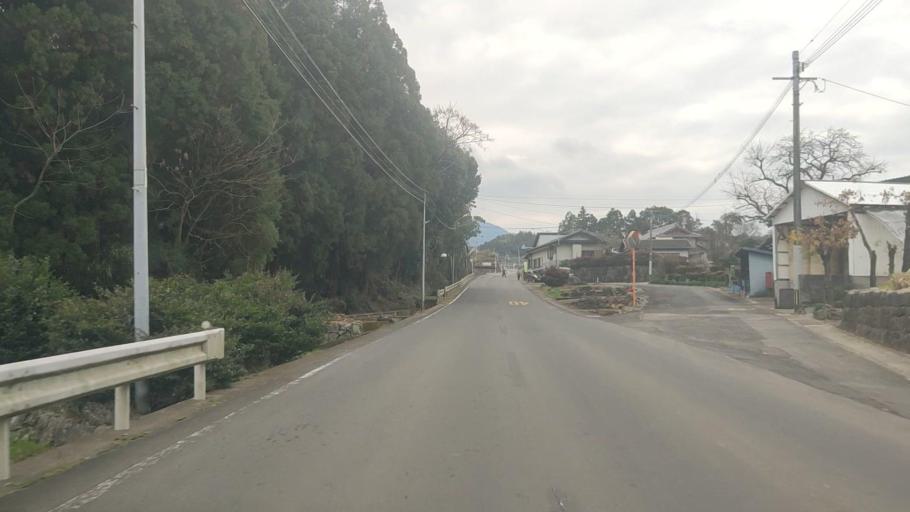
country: JP
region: Nagasaki
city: Shimabara
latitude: 32.8362
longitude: 130.2932
